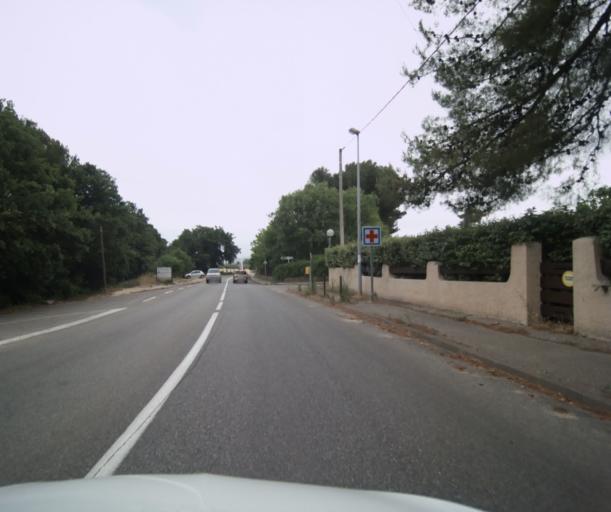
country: FR
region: Provence-Alpes-Cote d'Azur
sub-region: Departement du Var
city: Ollioules
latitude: 43.1320
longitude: 5.8754
